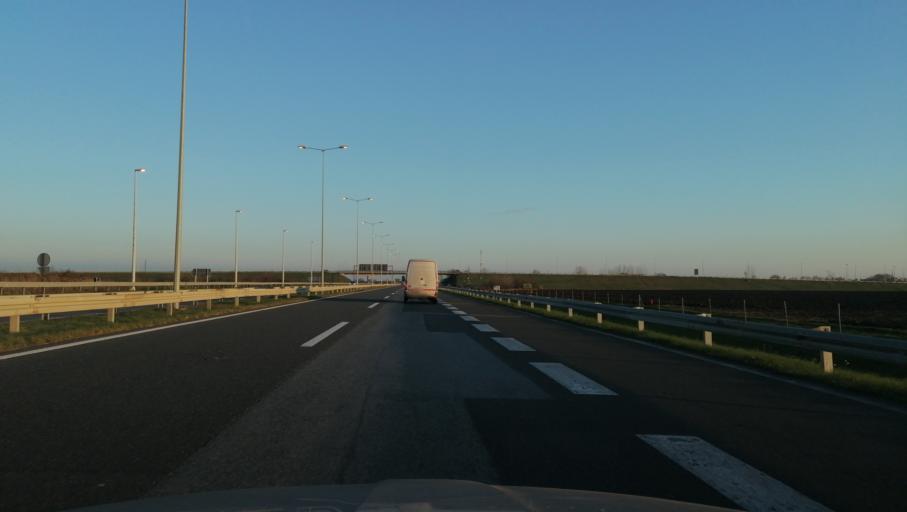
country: RS
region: Autonomna Pokrajina Vojvodina
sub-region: Sremski Okrug
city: Pecinci
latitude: 44.9215
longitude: 19.9544
